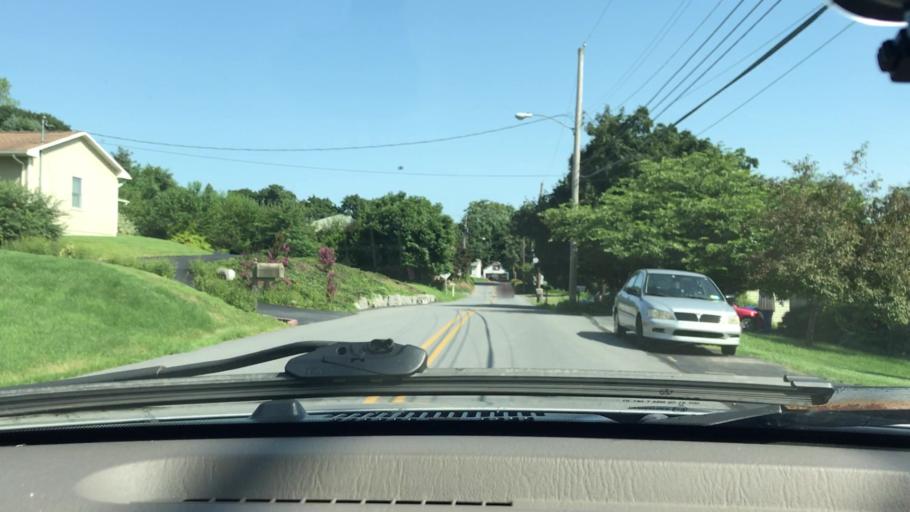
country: US
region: Pennsylvania
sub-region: Dauphin County
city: Rutherford
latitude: 40.2591
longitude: -76.7479
